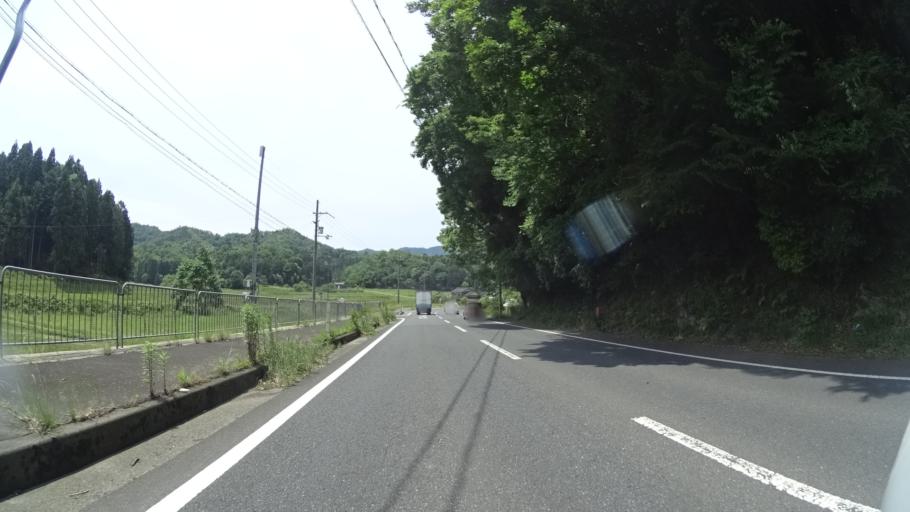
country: JP
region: Hyogo
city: Toyooka
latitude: 35.5736
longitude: 134.9847
